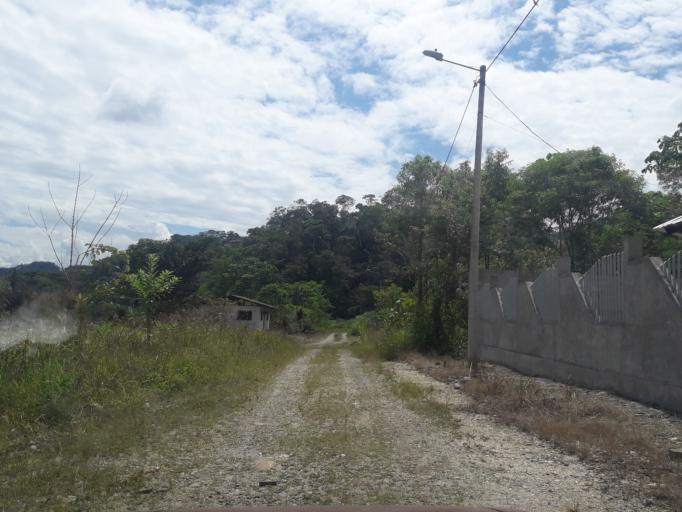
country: EC
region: Napo
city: Tena
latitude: -1.0182
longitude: -77.8624
